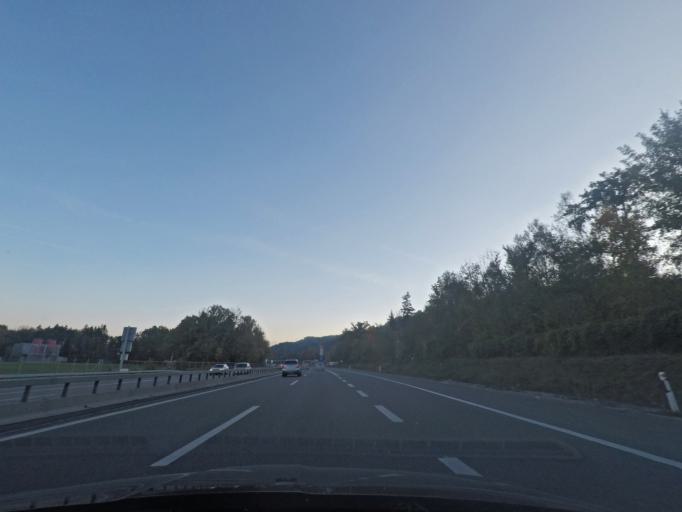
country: CH
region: Bern
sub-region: Bern-Mittelland District
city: Rubigen
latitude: 46.8815
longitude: 7.5413
